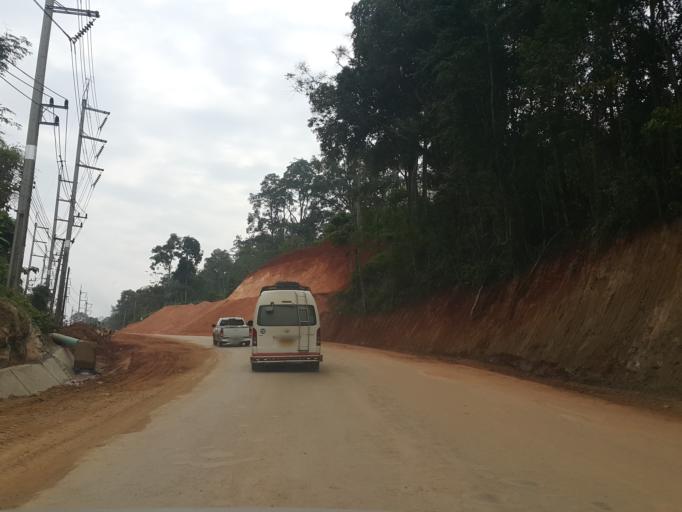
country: TH
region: Chiang Mai
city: Mae Taeng
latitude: 19.1387
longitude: 98.6987
